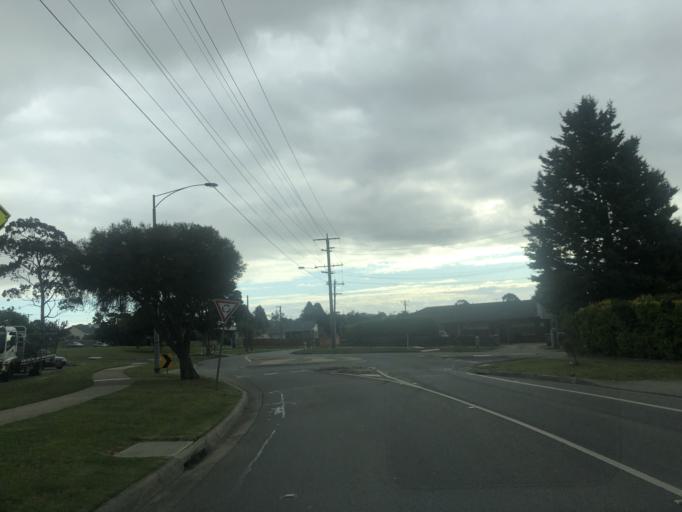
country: AU
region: Victoria
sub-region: Casey
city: Doveton
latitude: -37.9880
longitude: 145.2453
